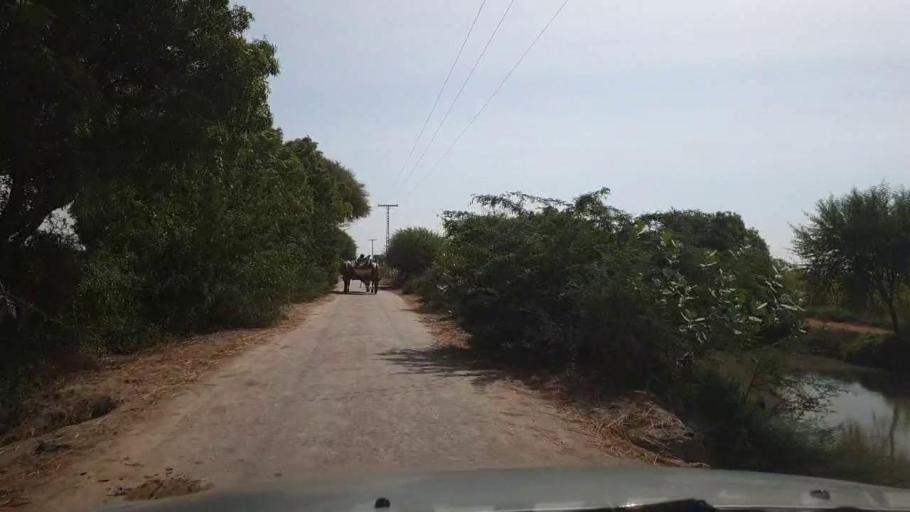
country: PK
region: Sindh
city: Tando Muhammad Khan
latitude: 25.1451
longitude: 68.3992
